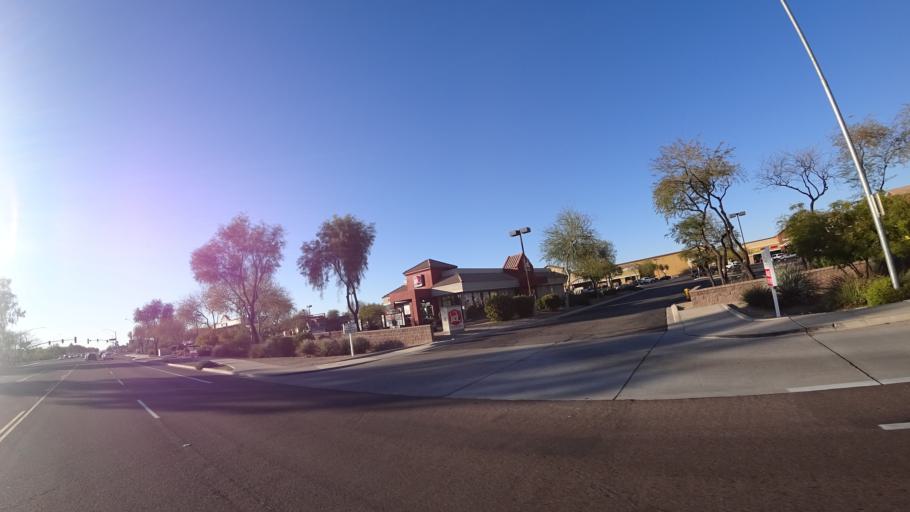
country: US
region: Arizona
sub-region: Maricopa County
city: Sun City
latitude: 33.6816
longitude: -112.2359
